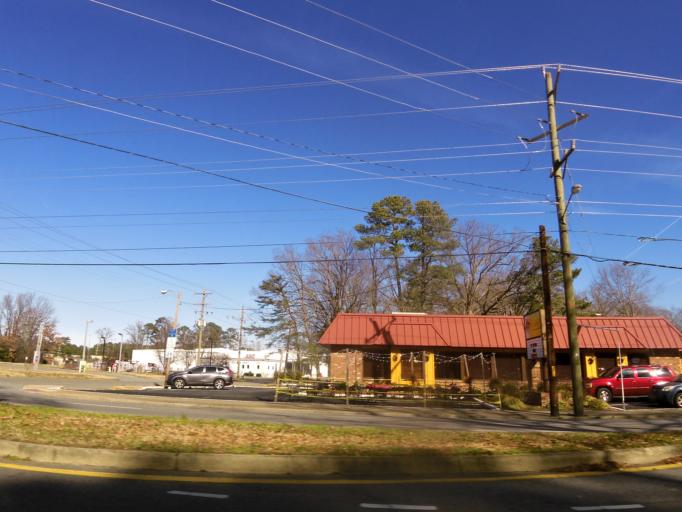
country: US
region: Virginia
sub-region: City of Newport News
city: Newport News
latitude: 37.0365
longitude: -76.4663
